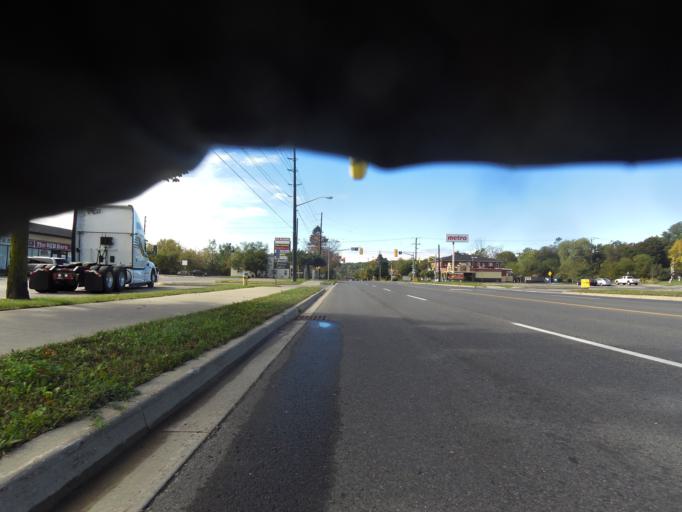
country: CA
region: Ontario
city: Cobourg
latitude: 43.9496
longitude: -78.2847
